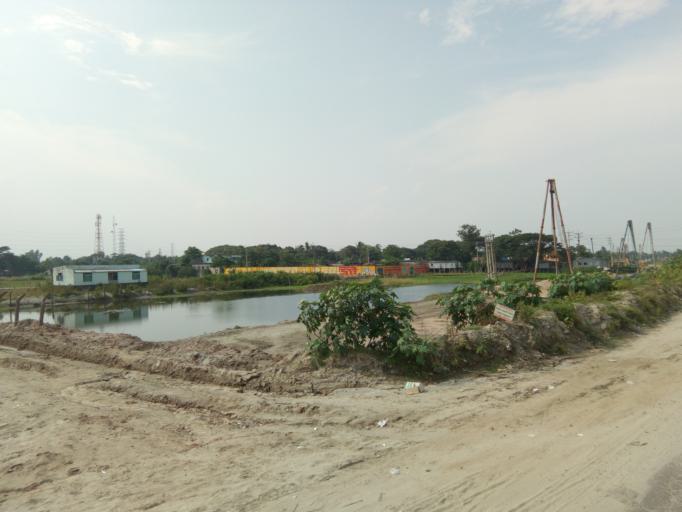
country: BD
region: Dhaka
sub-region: Dhaka
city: Dhaka
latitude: 23.6506
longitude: 90.3504
